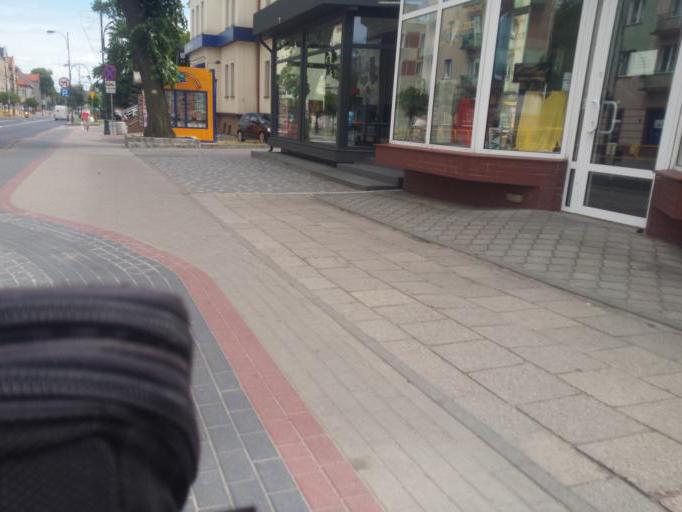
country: PL
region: Warmian-Masurian Voivodeship
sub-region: Powiat ilawski
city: Ilawa
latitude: 53.5972
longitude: 19.5622
